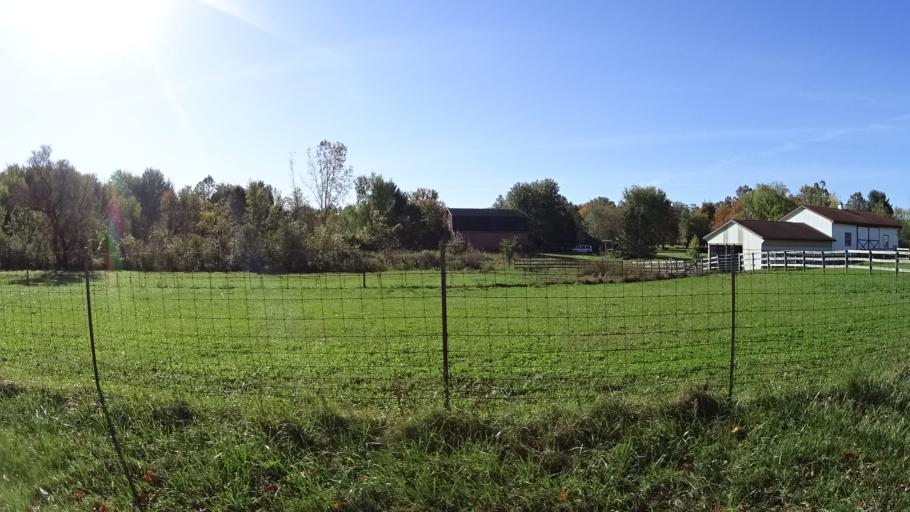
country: US
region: Ohio
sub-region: Lorain County
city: Vermilion-on-the-Lake
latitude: 41.3959
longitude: -82.3235
